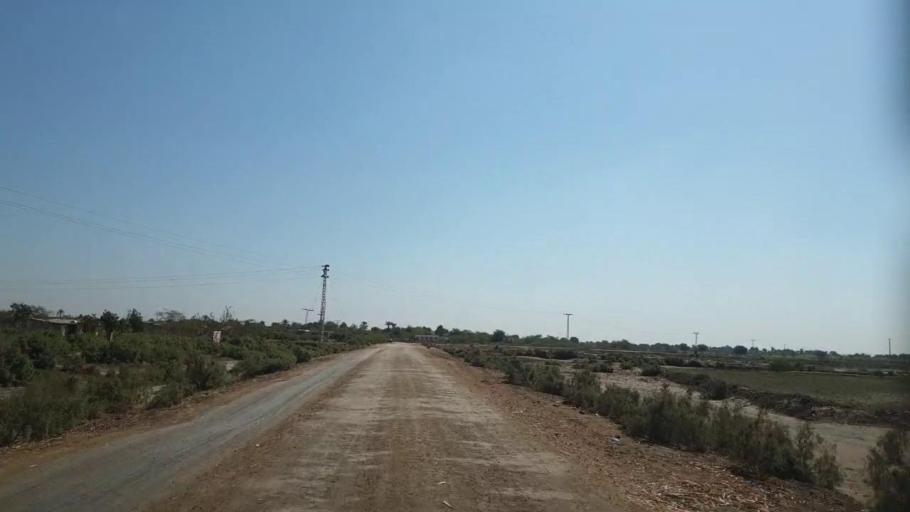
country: PK
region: Sindh
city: Mirpur Khas
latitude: 25.5841
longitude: 69.1112
